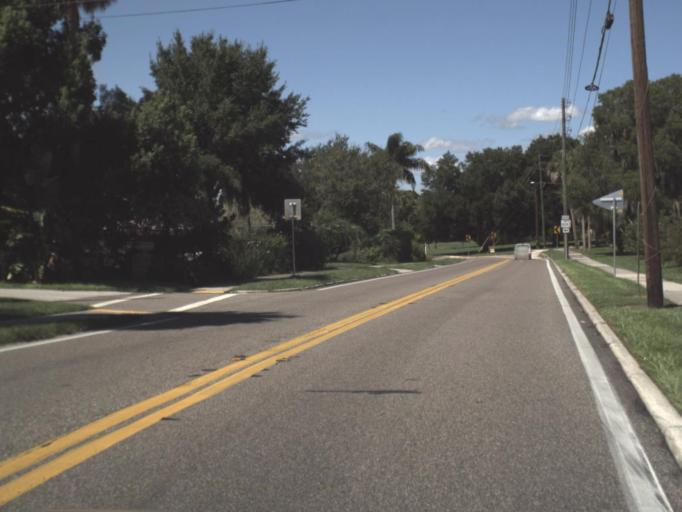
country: US
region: Florida
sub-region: Polk County
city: Auburndale
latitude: 28.0885
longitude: -81.7899
